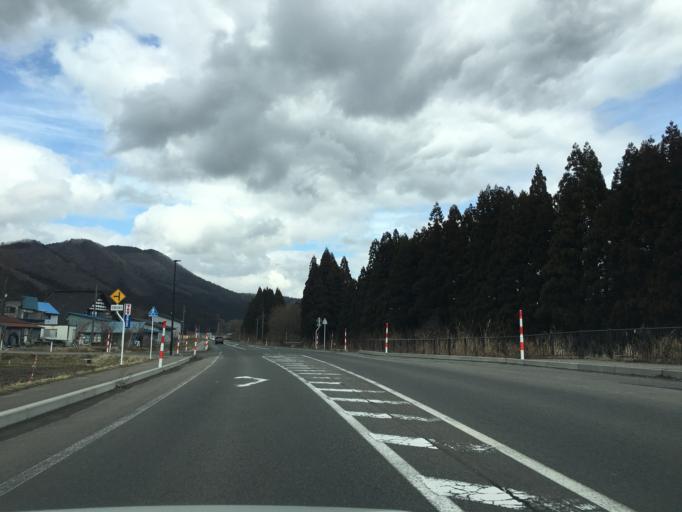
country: JP
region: Akita
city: Hanawa
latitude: 40.2241
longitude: 140.6773
